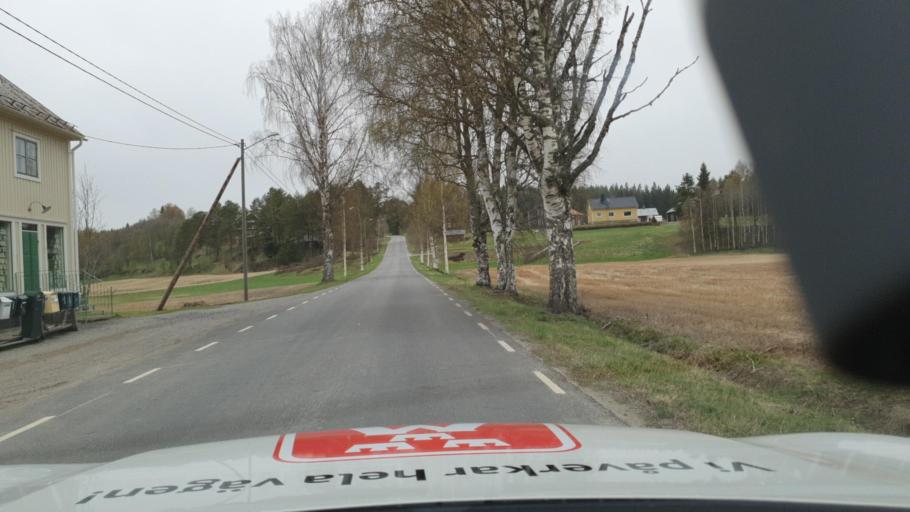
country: SE
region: Vaesterbotten
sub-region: Nordmalings Kommun
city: Nordmaling
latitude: 63.7268
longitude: 19.5111
